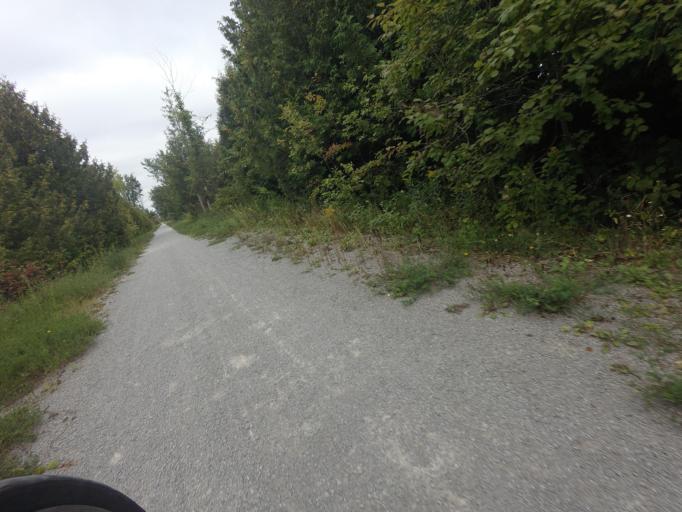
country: CA
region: Ontario
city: Omemee
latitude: 44.3170
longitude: -78.8517
